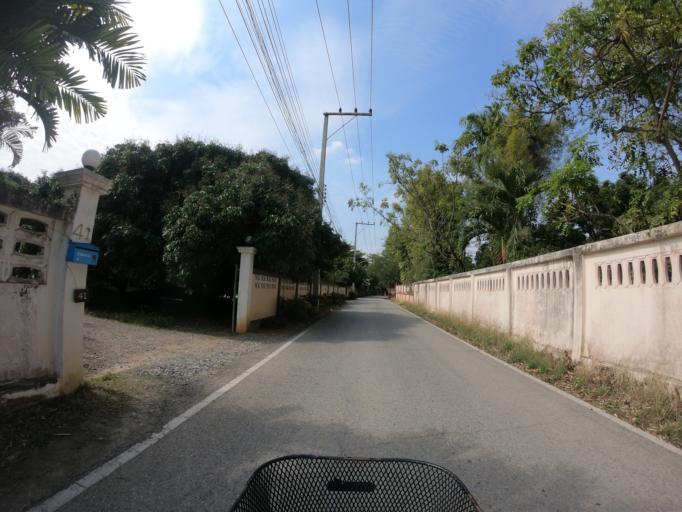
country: TH
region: Chiang Mai
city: Saraphi
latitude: 18.7083
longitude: 99.0220
